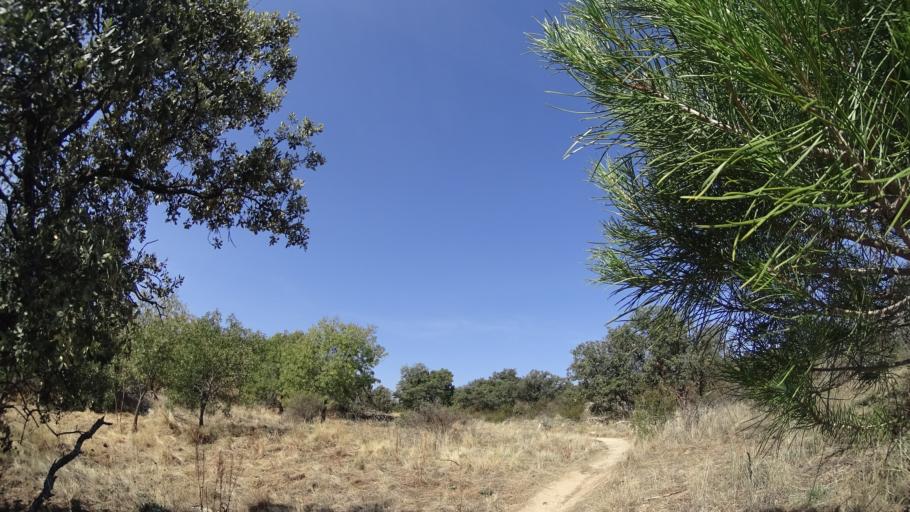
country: ES
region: Madrid
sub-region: Provincia de Madrid
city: Galapagar
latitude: 40.5844
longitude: -3.9763
